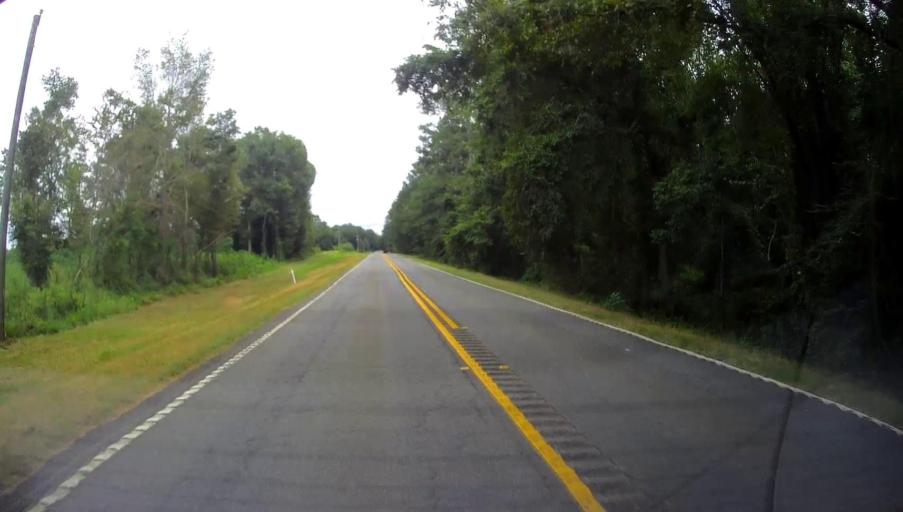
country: US
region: Georgia
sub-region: Macon County
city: Montezuma
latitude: 32.2929
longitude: -83.9117
